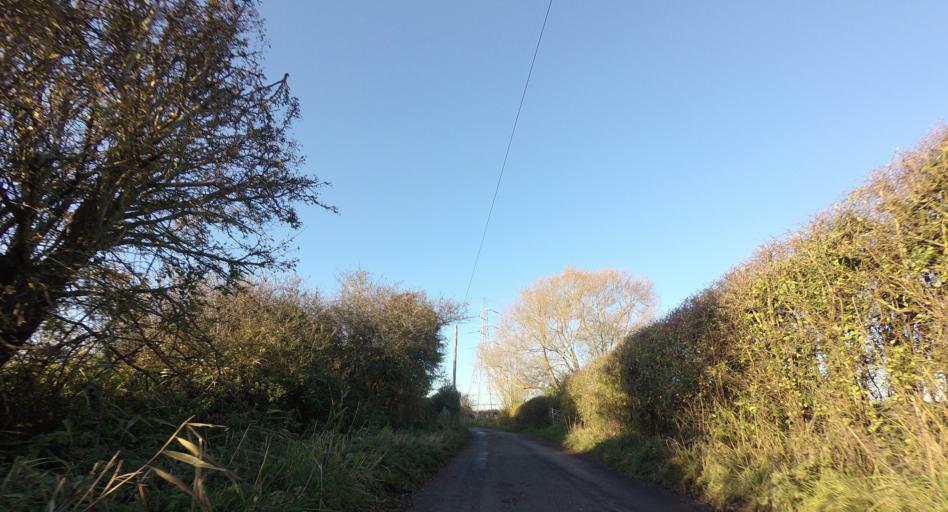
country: GB
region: England
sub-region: West Sussex
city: Steyning
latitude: 50.8934
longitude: -0.3131
